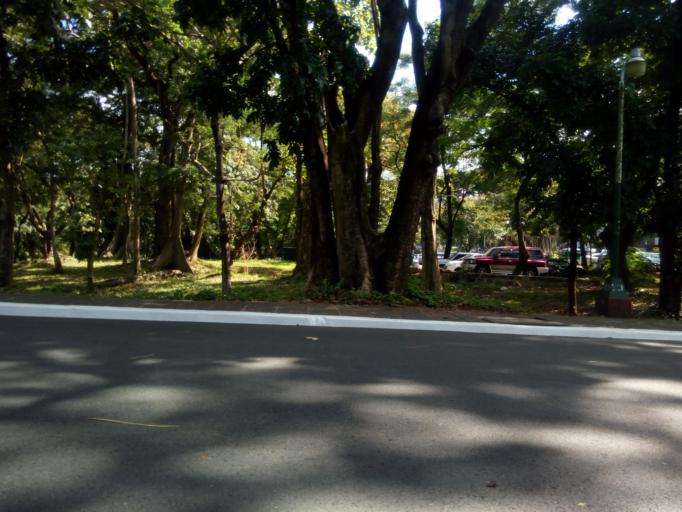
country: PH
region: Metro Manila
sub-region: Quezon City
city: Quezon City
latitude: 14.6544
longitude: 121.0686
